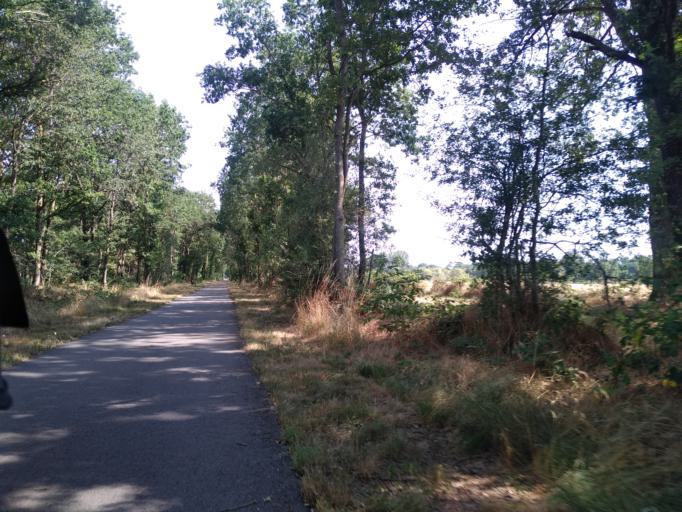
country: FR
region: Bourgogne
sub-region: Departement de Saone-et-Loire
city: Marcigny
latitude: 46.3360
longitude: 4.0284
